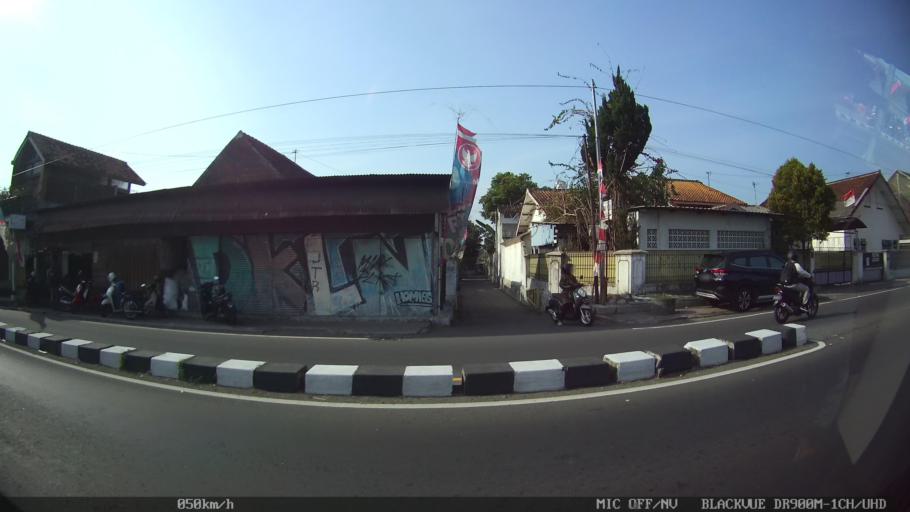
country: ID
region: Daerah Istimewa Yogyakarta
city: Kasihan
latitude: -7.8271
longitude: 110.3521
